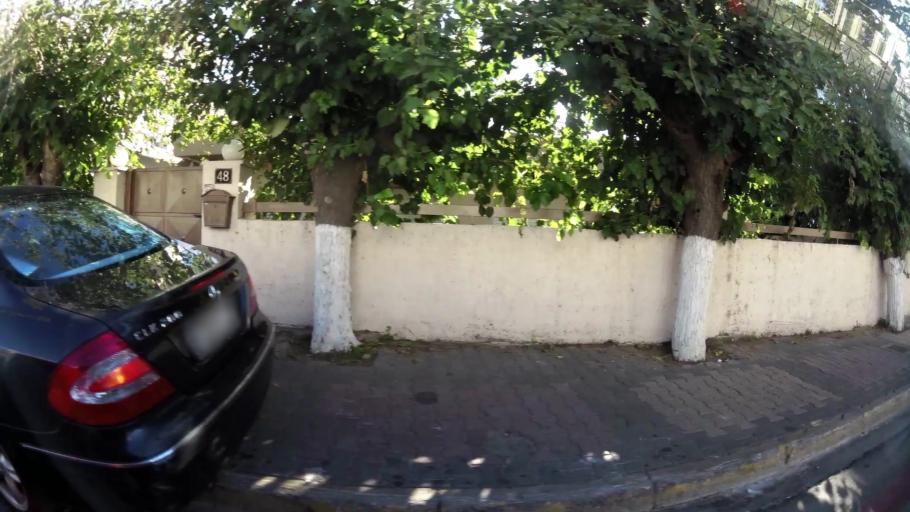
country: GR
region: Attica
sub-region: Nomarchia Anatolikis Attikis
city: Pallini
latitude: 38.0037
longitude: 23.8767
